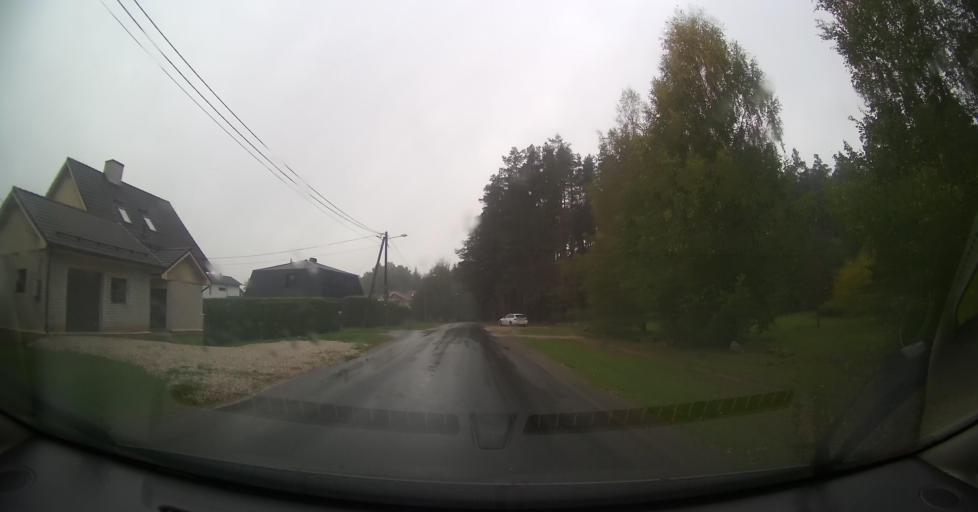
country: EE
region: Tartu
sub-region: Tartu linn
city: Tartu
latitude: 58.3592
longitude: 26.7903
